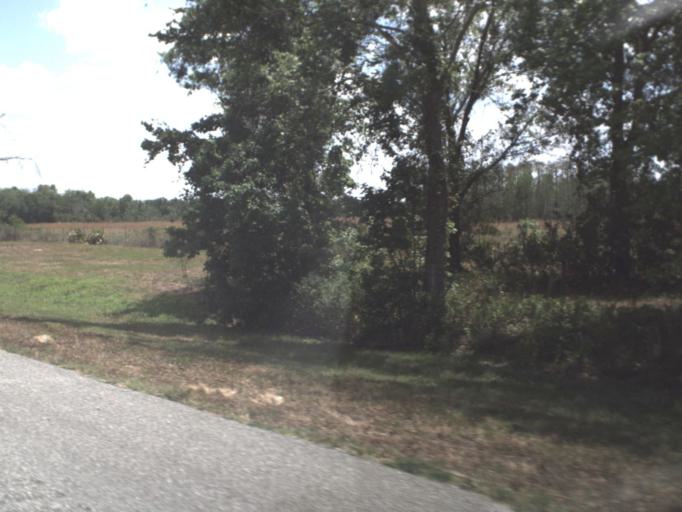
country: US
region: Florida
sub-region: Orange County
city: Wedgefield
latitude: 28.4517
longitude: -81.0781
